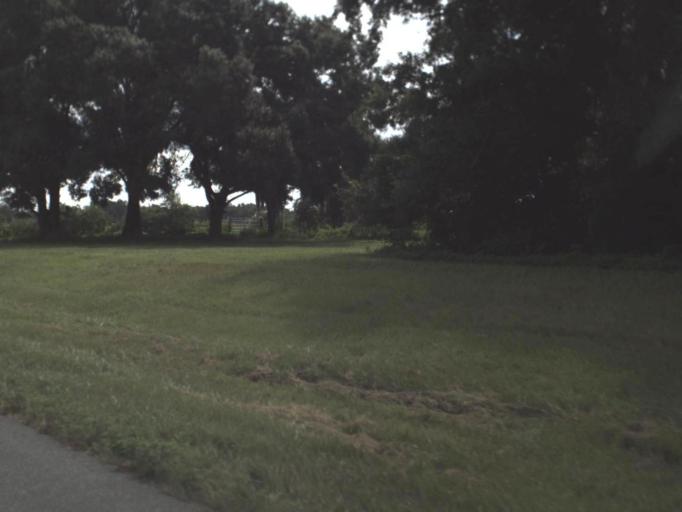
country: US
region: Florida
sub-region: Pasco County
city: Zephyrhills South
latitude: 28.2030
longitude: -82.1903
